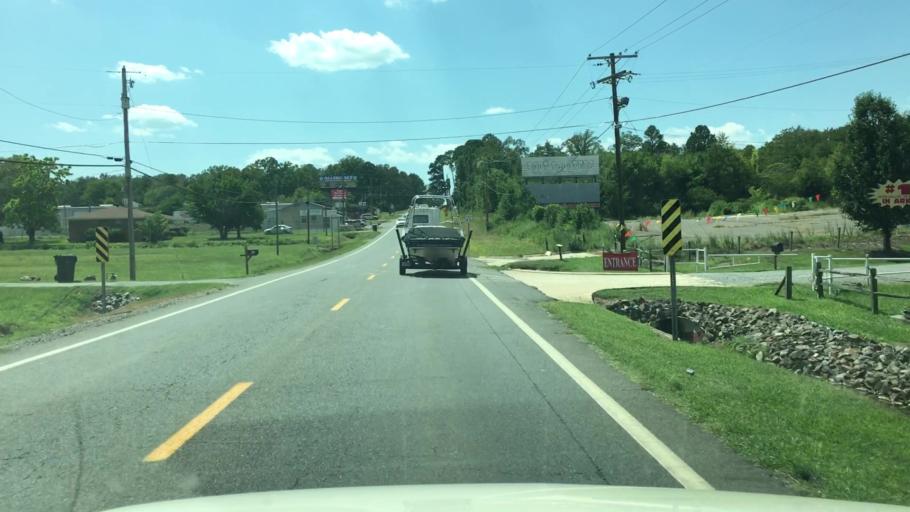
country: US
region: Arkansas
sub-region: Garland County
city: Piney
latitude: 34.5078
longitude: -93.1349
